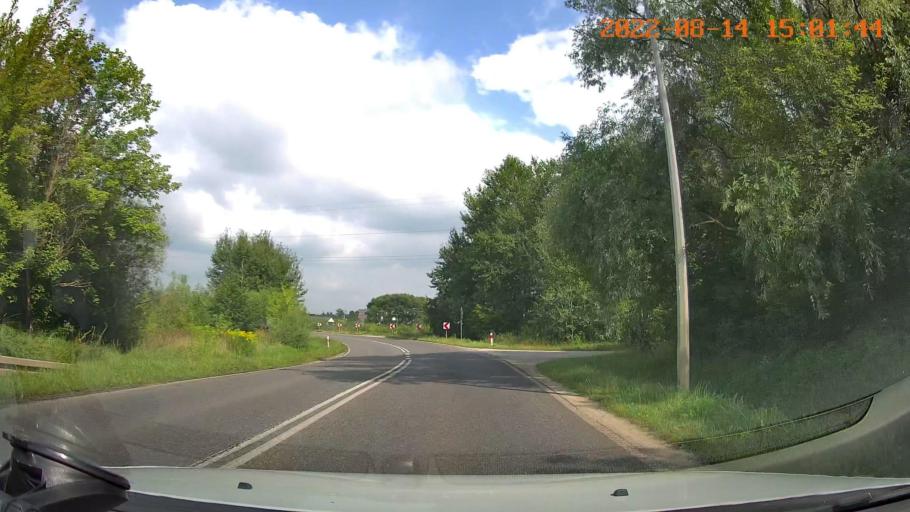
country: PL
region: Swietokrzyskie
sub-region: Powiat kielecki
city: Piekoszow
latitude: 50.8812
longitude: 20.5136
